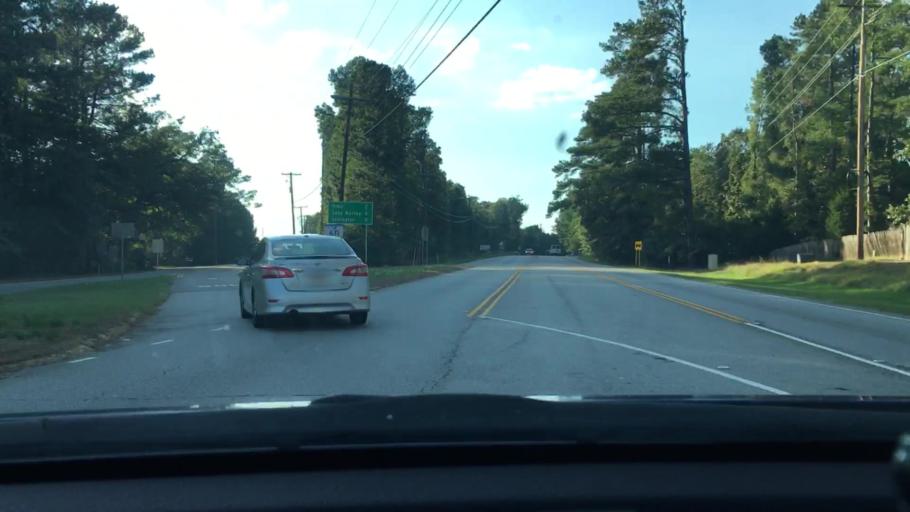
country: US
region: South Carolina
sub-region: Lexington County
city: Seven Oaks
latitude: 34.0866
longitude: -81.1448
